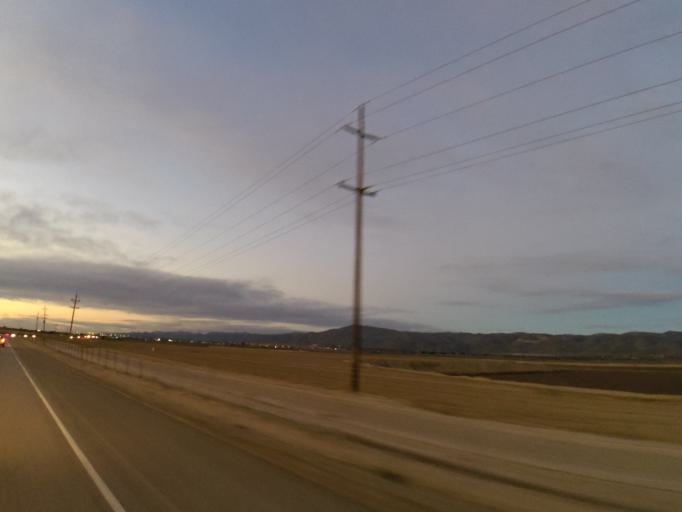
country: US
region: California
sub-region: Monterey County
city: Soledad
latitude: 36.3852
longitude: -121.3022
